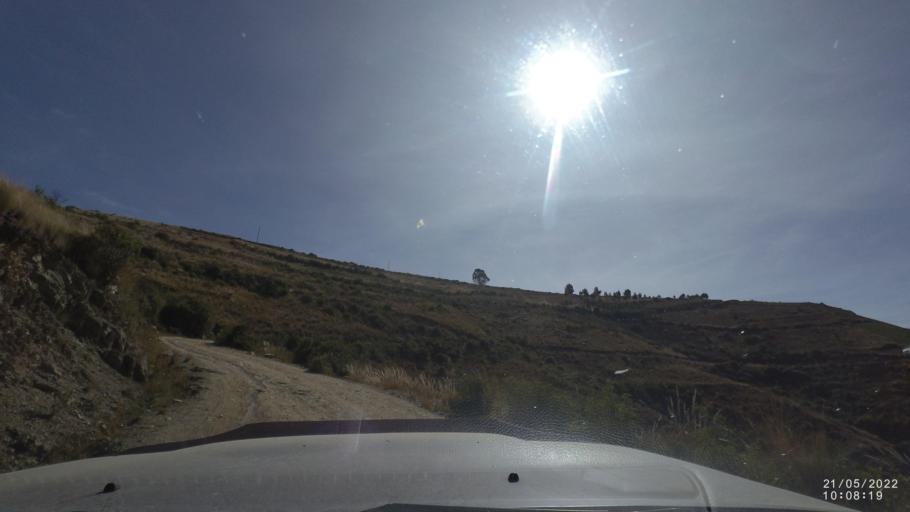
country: BO
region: Cochabamba
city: Colomi
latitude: -17.3379
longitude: -65.9864
